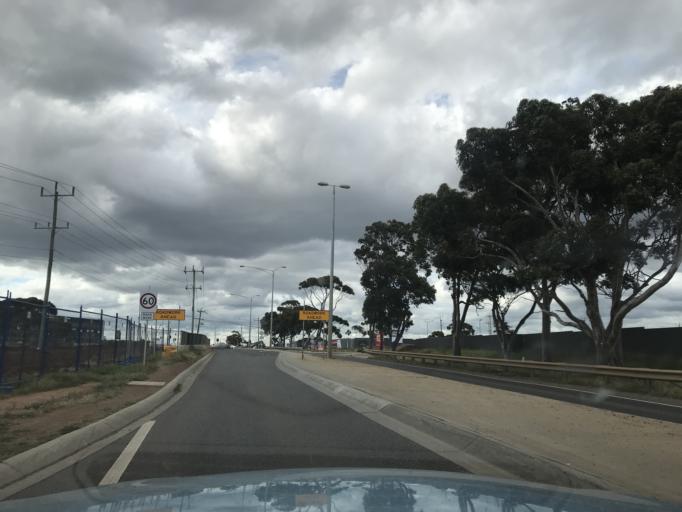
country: AU
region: Victoria
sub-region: Wyndham
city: Williams Landing
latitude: -37.8413
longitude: 144.7467
